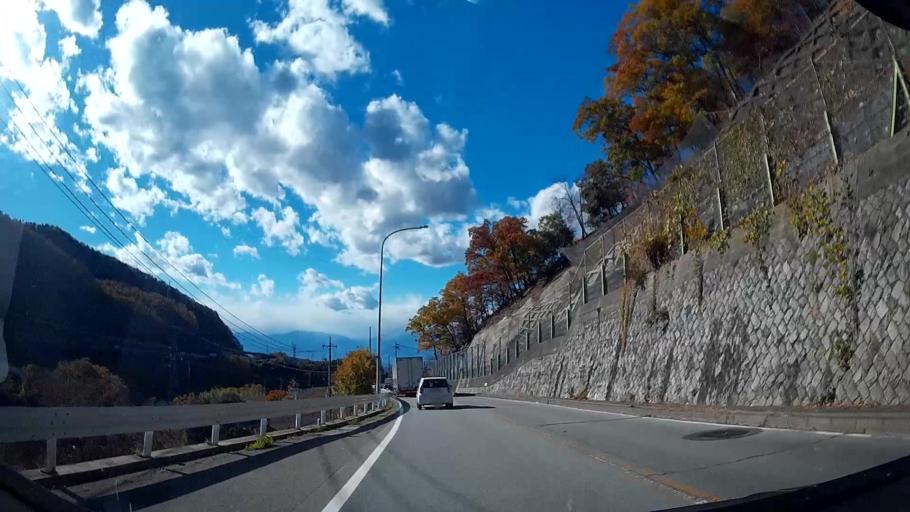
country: JP
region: Yamanashi
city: Enzan
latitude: 35.6548
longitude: 138.7471
